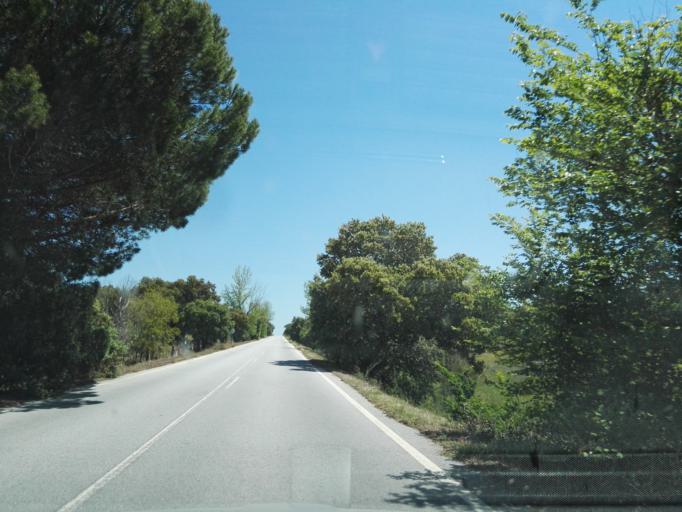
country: PT
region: Portalegre
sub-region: Elvas
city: Elvas
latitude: 38.9973
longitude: -7.1826
